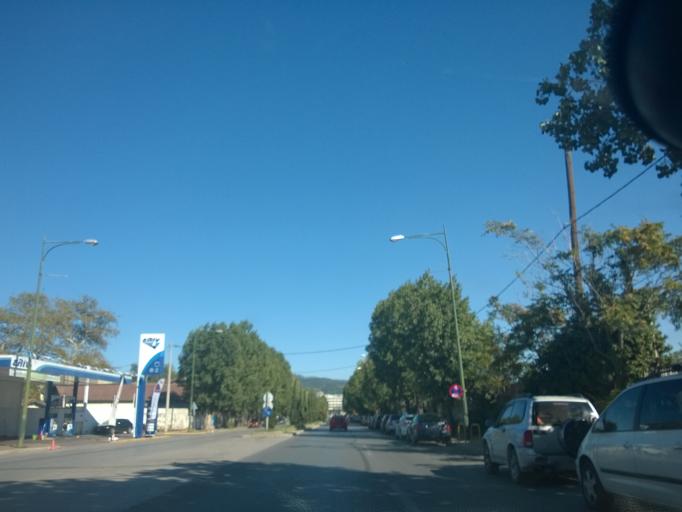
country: GR
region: Central Macedonia
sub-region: Nomos Thessalonikis
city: Thessaloniki
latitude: 40.6400
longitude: 22.9240
